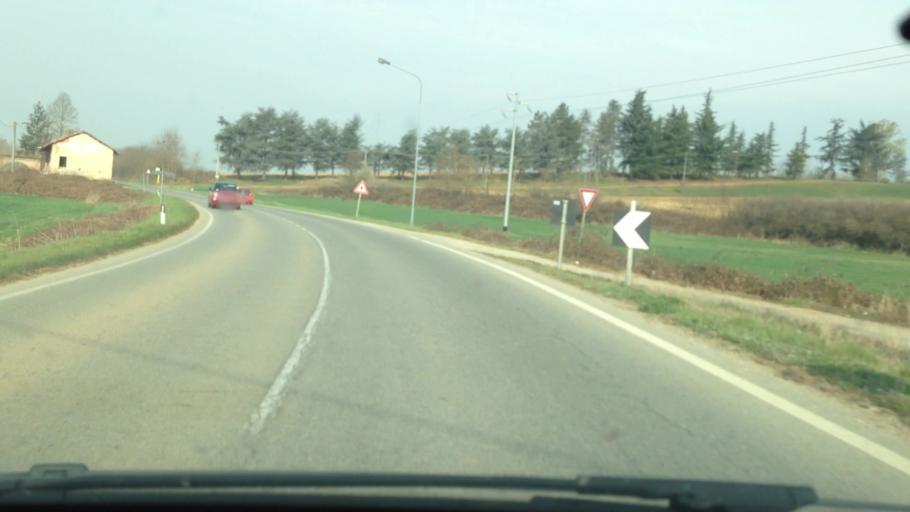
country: IT
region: Piedmont
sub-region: Provincia di Torino
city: Pralormo
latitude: 44.8360
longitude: 7.9220
